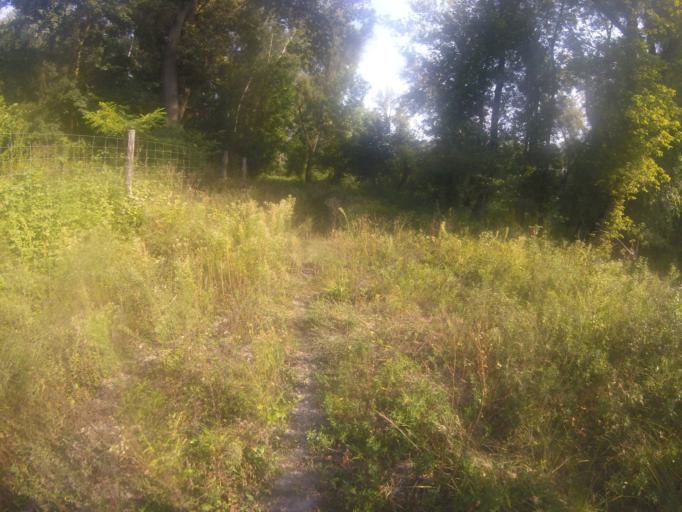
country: HU
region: Bacs-Kiskun
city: Baja
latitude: 46.1840
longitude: 18.9209
